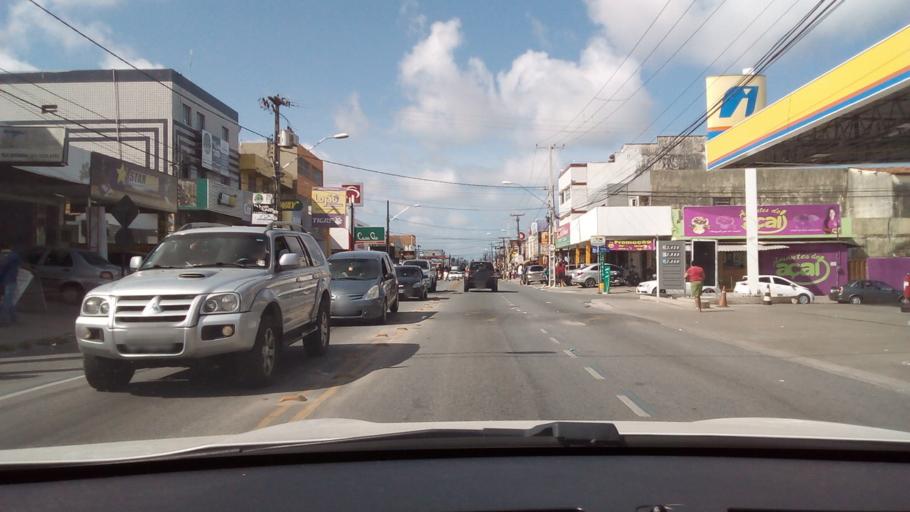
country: BR
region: Paraiba
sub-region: Joao Pessoa
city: Joao Pessoa
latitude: -7.1693
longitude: -34.8386
